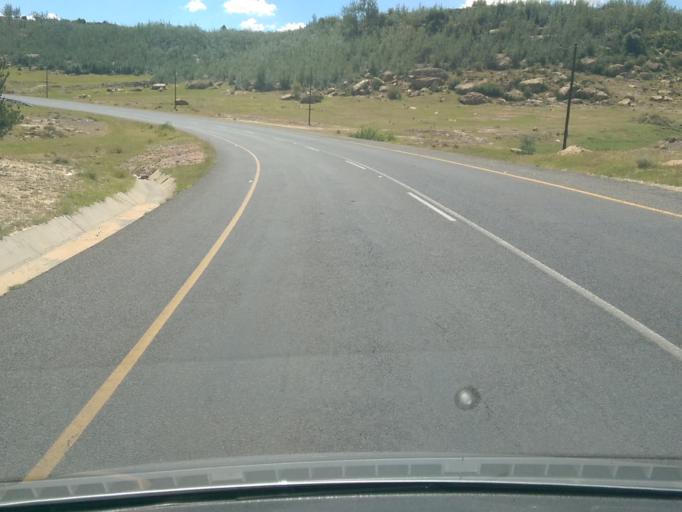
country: LS
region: Maseru
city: Maseru
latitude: -29.3951
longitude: 27.5296
